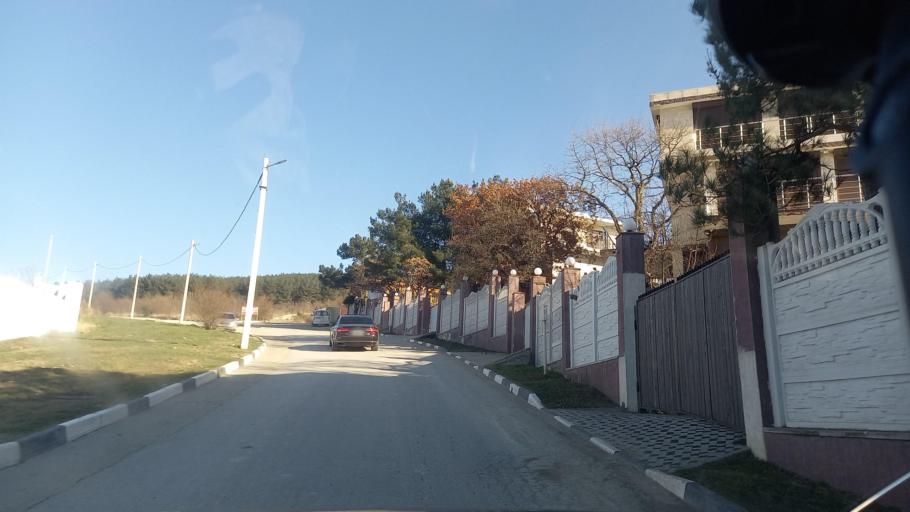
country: RU
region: Krasnodarskiy
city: Kabardinka
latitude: 44.6300
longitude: 37.9092
